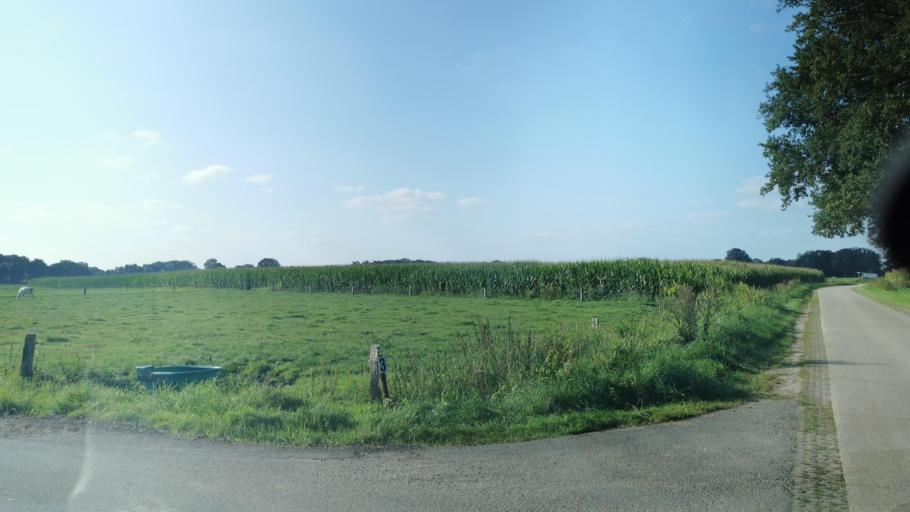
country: NL
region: Overijssel
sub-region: Gemeente Borne
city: Borne
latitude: 52.3413
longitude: 6.8021
